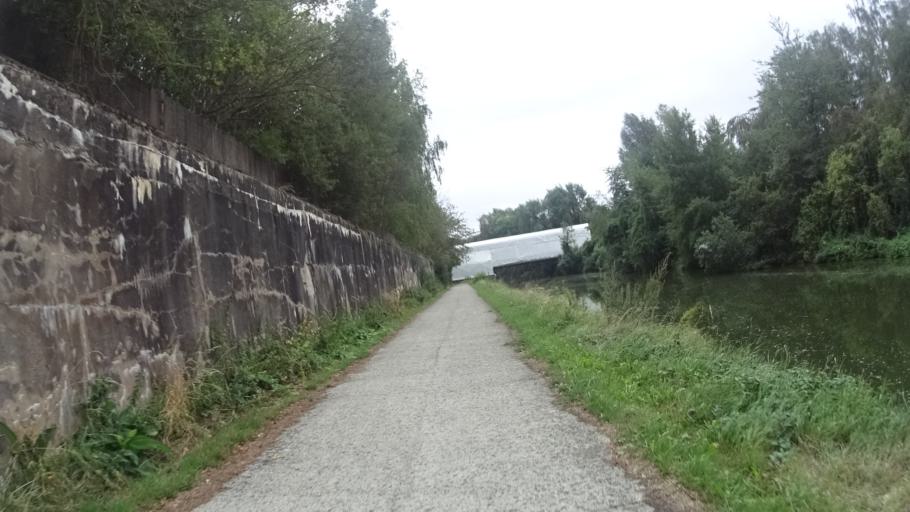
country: FR
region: Nord-Pas-de-Calais
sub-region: Departement du Nord
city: Hautmont
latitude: 50.2644
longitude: 3.9311
